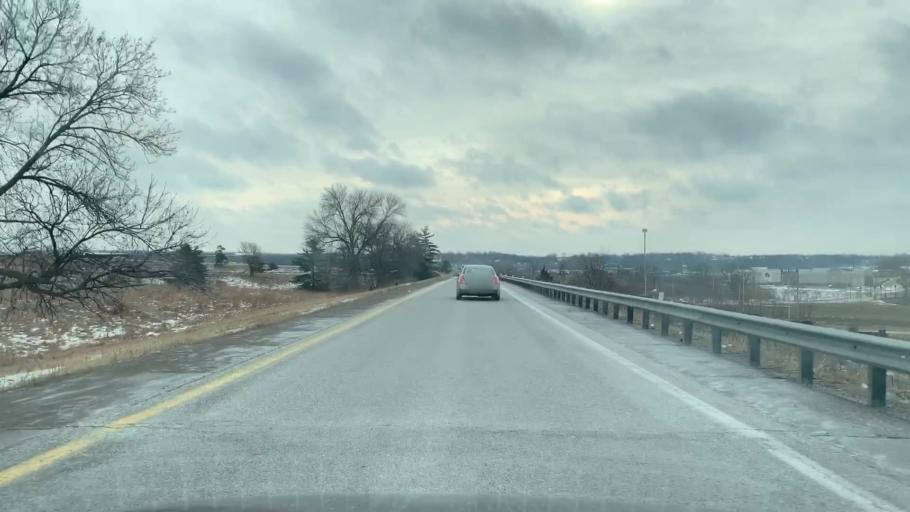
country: US
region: Missouri
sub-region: Jackson County
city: East Independence
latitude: 39.0417
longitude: -94.3673
